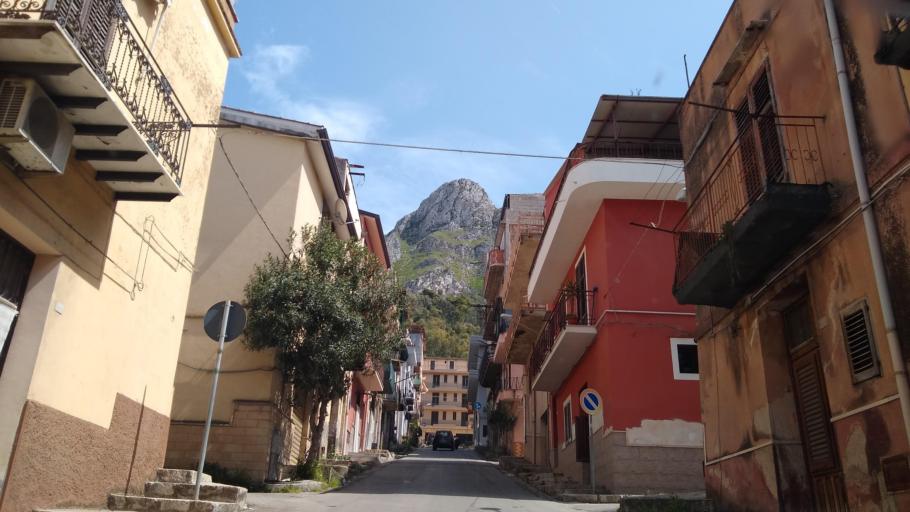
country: IT
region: Sicily
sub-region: Palermo
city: San Giuseppe Jato
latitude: 37.9716
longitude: 13.1821
